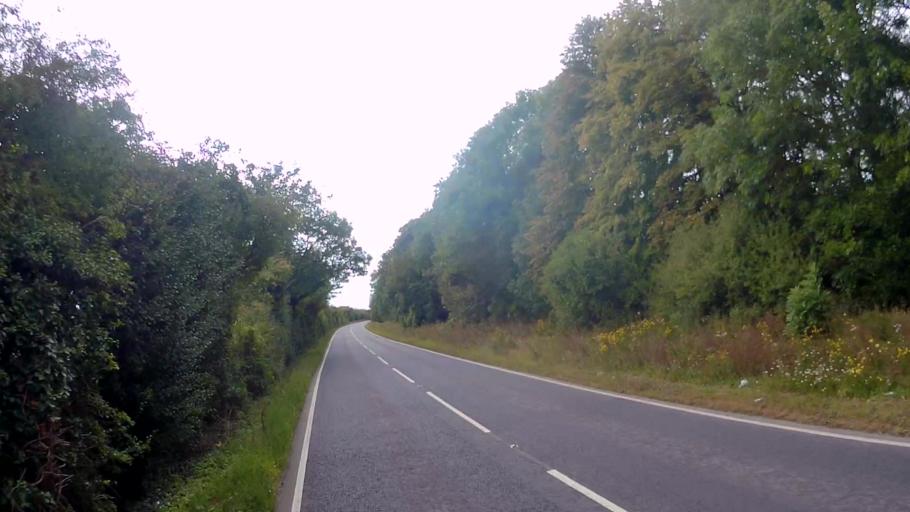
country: GB
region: England
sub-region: Hampshire
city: Overton
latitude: 51.1861
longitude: -1.2673
